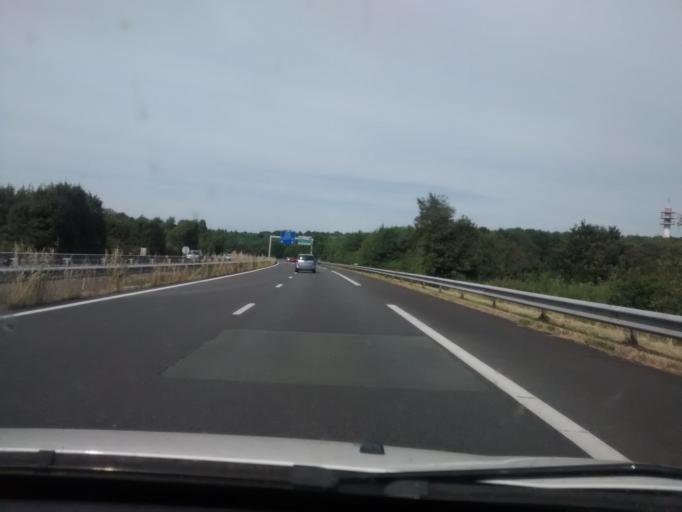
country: FR
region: Pays de la Loire
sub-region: Departement de la Sarthe
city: Rouillon
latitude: 48.0174
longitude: 0.1261
